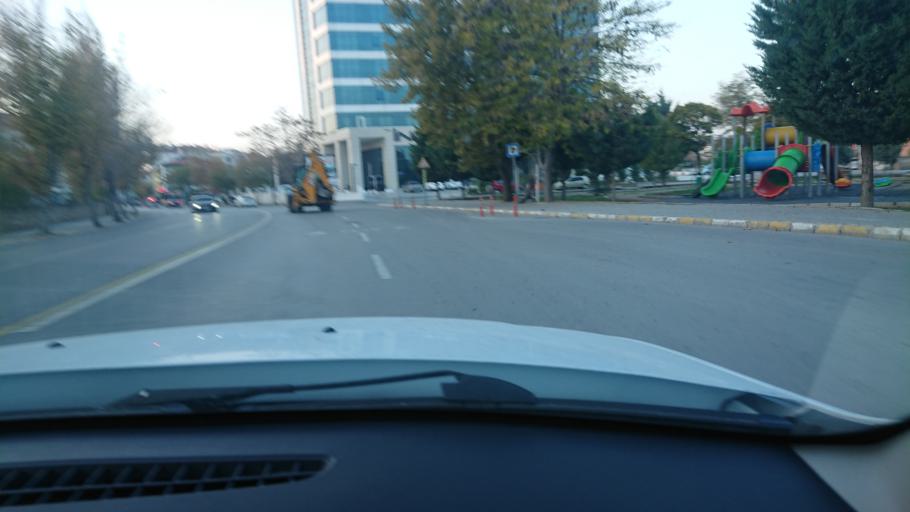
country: TR
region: Aksaray
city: Aksaray
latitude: 38.3581
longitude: 34.0409
